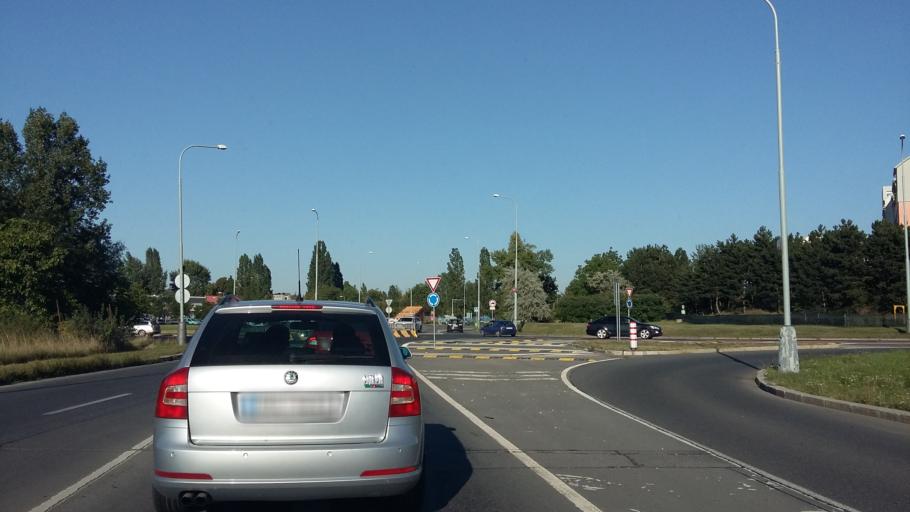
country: CZ
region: Praha
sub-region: Praha 18
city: Letnany
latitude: 50.1421
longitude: 14.5045
